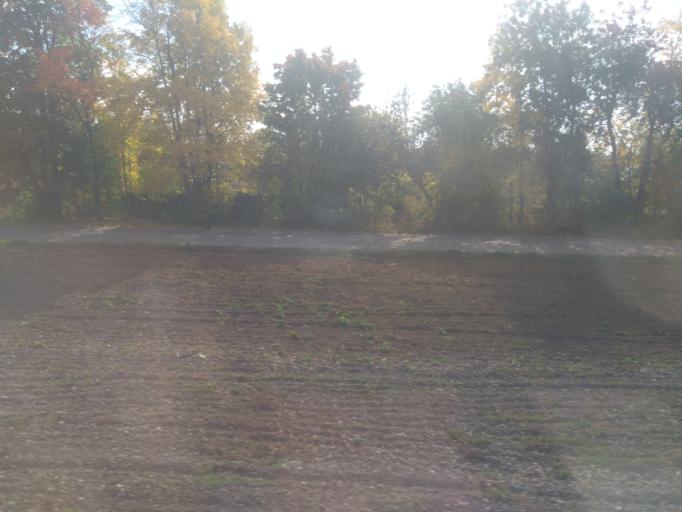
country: RU
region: Tatarstan
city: Aysha
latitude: 55.8418
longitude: 48.5853
